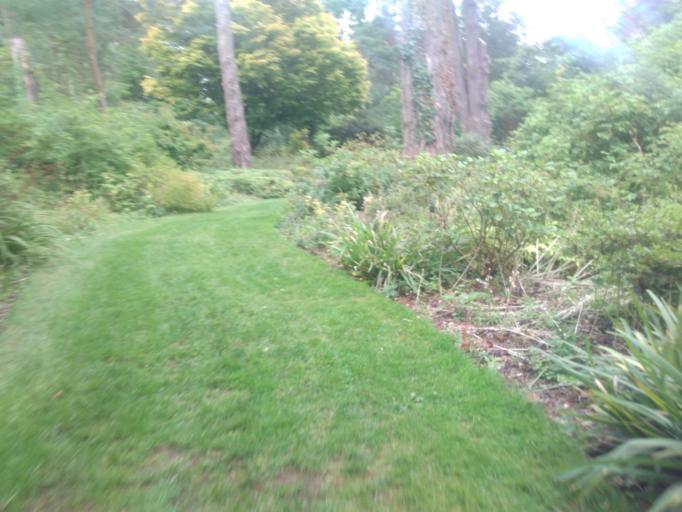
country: GB
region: England
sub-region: Devon
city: Tiverton
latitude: 50.9257
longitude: -3.4793
